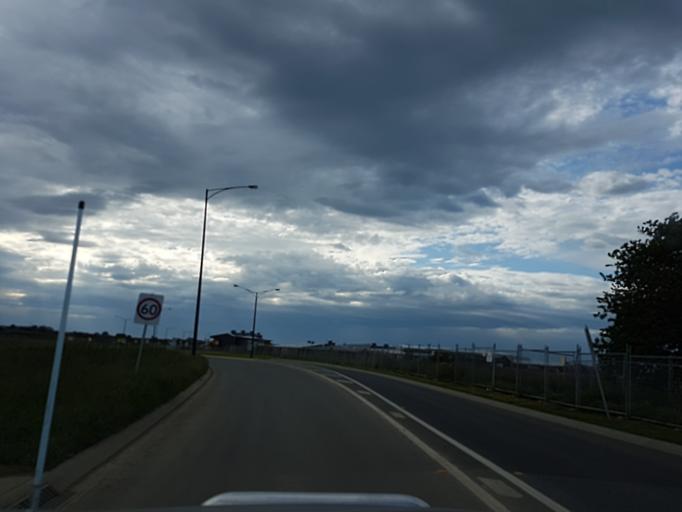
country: AU
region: Victoria
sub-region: Cardinia
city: Officer
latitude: -38.0694
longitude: 145.4083
